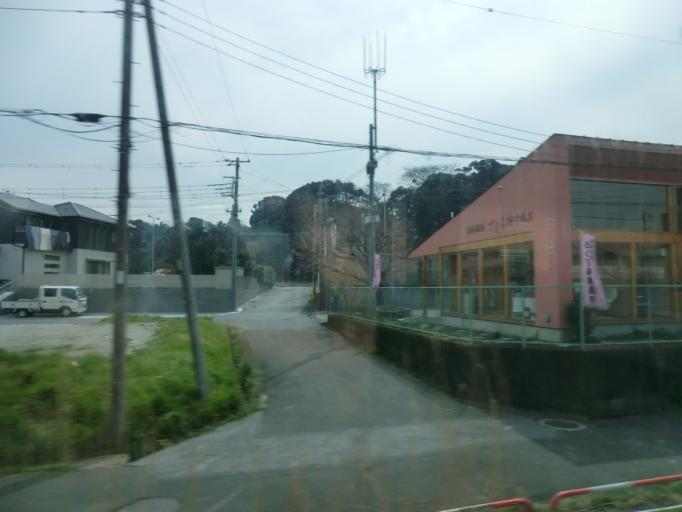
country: JP
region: Chiba
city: Kisarazu
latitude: 35.3659
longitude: 139.9234
